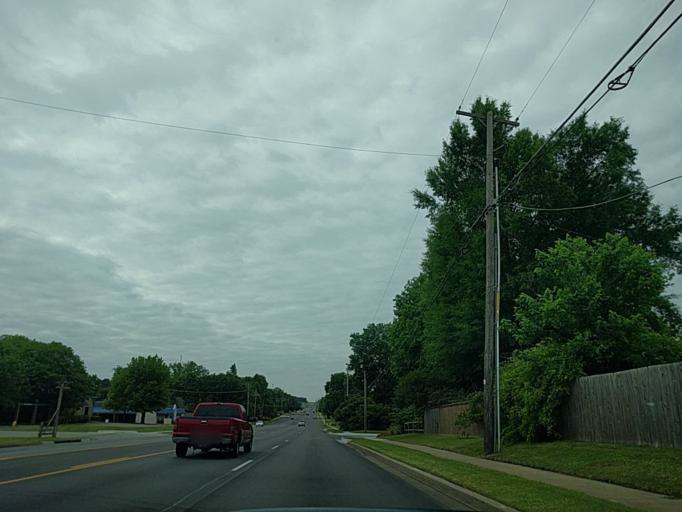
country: US
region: Oklahoma
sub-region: Tulsa County
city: Jenks
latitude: 36.0874
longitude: -95.9045
